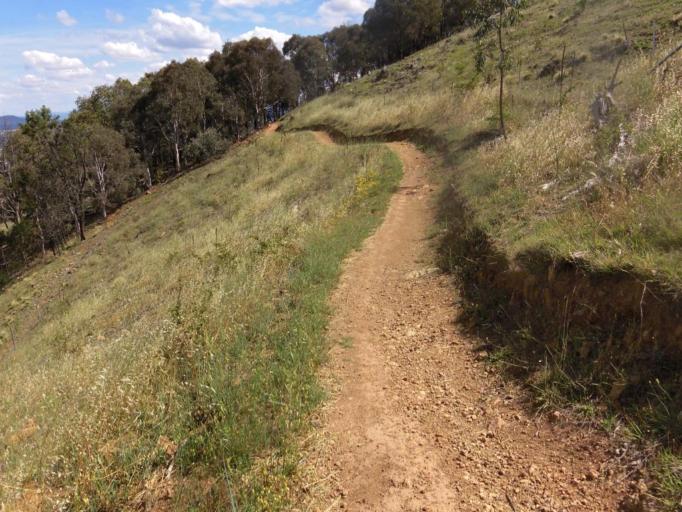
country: AU
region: Australian Capital Territory
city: Belconnen
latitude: -35.1445
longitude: 149.0922
